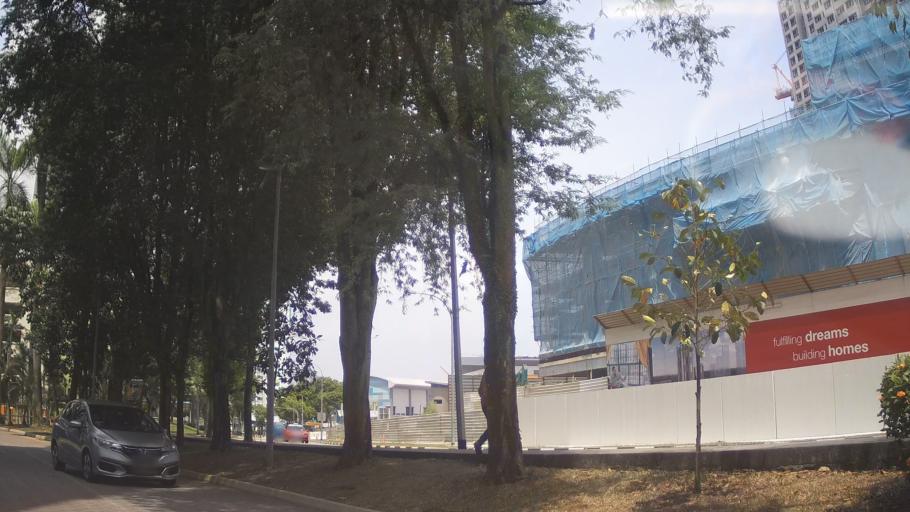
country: MY
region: Johor
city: Johor Bahru
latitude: 1.3866
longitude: 103.7619
